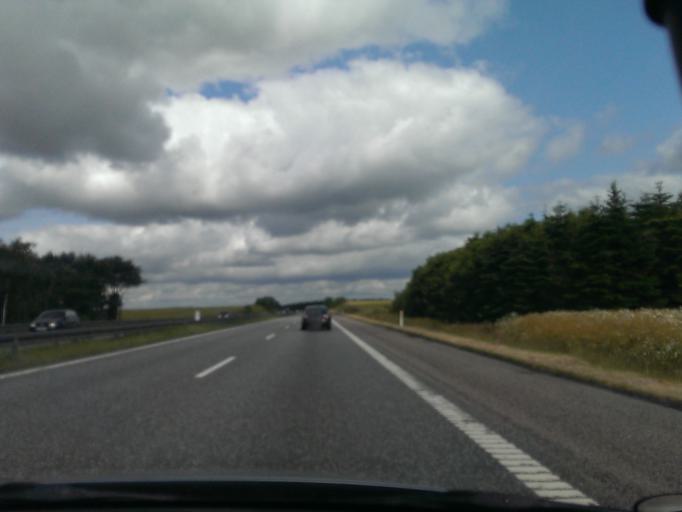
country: DK
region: North Denmark
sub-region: Mariagerfjord Kommune
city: Hobro
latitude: 56.5613
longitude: 9.8648
